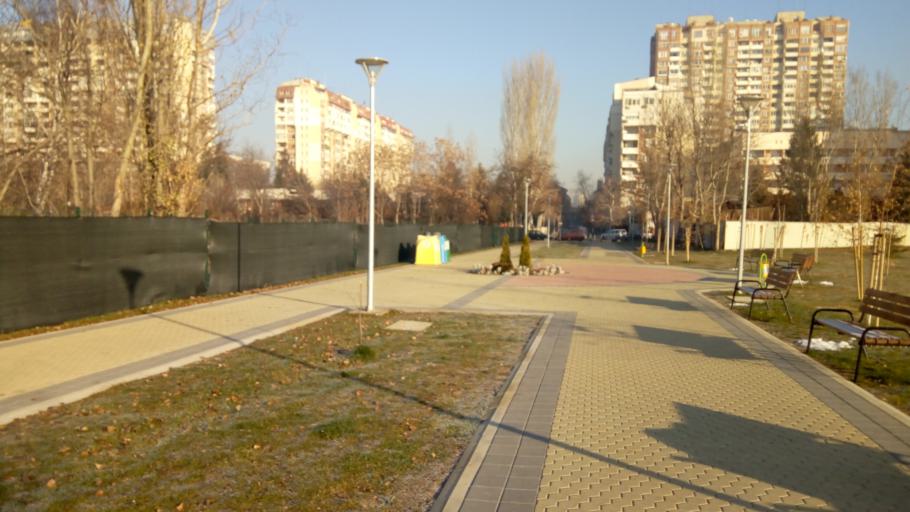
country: BG
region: Sofia-Capital
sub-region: Stolichna Obshtina
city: Sofia
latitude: 42.6956
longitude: 23.3069
